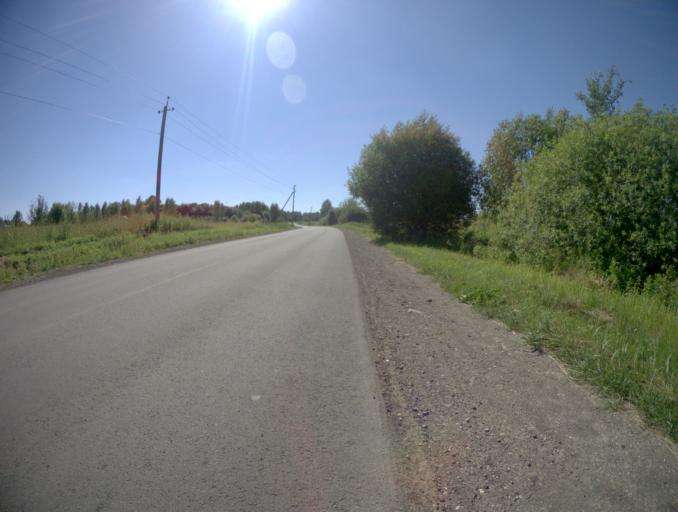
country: RU
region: Nizjnij Novgorod
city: Vorsma
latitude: 56.0466
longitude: 43.2148
